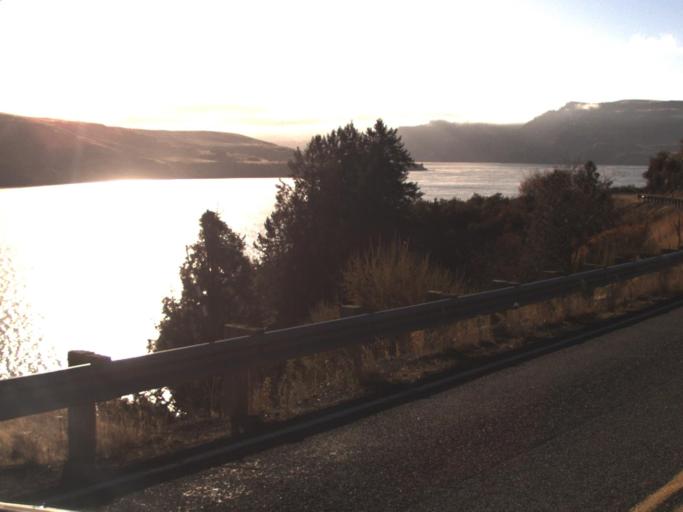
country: US
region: Washington
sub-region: Okanogan County
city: Coulee Dam
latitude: 47.9705
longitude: -118.7005
